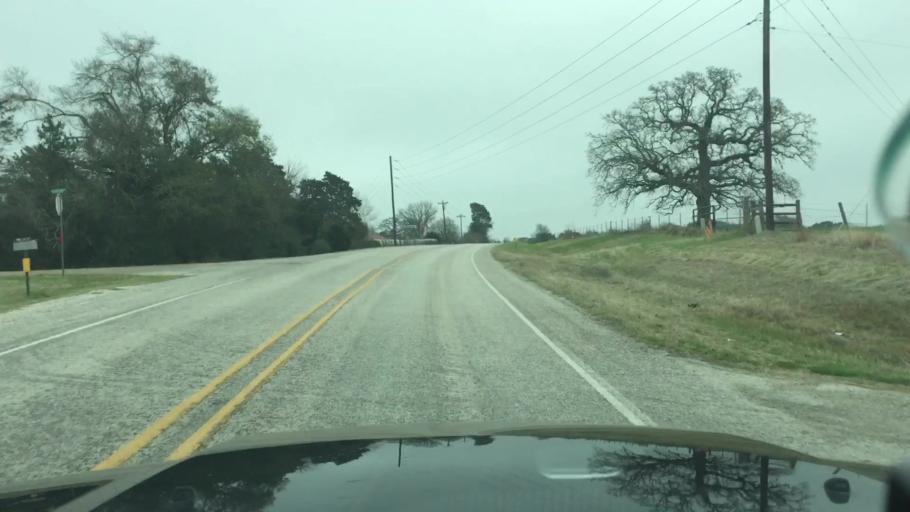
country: US
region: Texas
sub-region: Fayette County
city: La Grange
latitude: 30.0061
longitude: -96.9052
